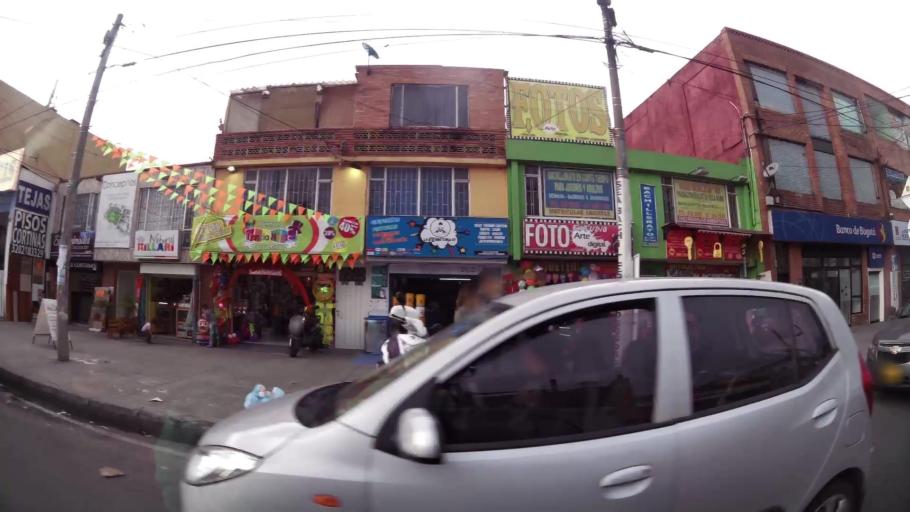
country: CO
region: Bogota D.C.
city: Barrio San Luis
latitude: 4.7162
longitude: -74.0588
